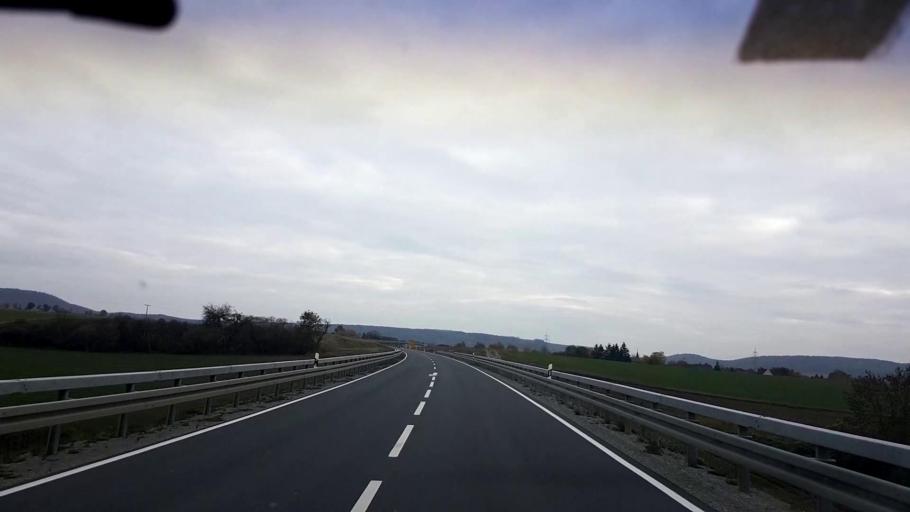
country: DE
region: Bavaria
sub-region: Regierungsbezirk Unterfranken
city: Castell
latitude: 49.7700
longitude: 10.3464
